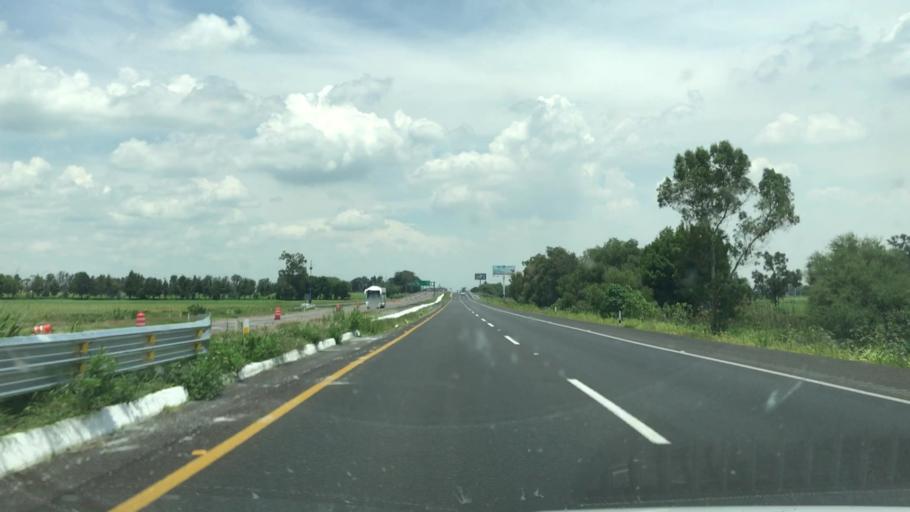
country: MX
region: Guanajuato
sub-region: Irapuato
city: Cuarta Brigada
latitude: 20.6526
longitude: -101.2864
